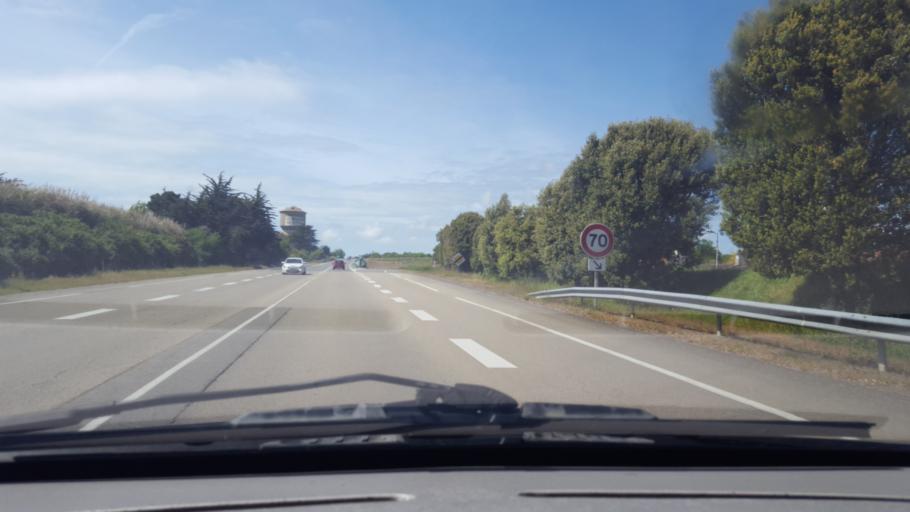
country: FR
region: Pays de la Loire
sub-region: Departement de la Loire-Atlantique
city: Les Moutiers-en-Retz
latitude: 47.0632
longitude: -1.9820
